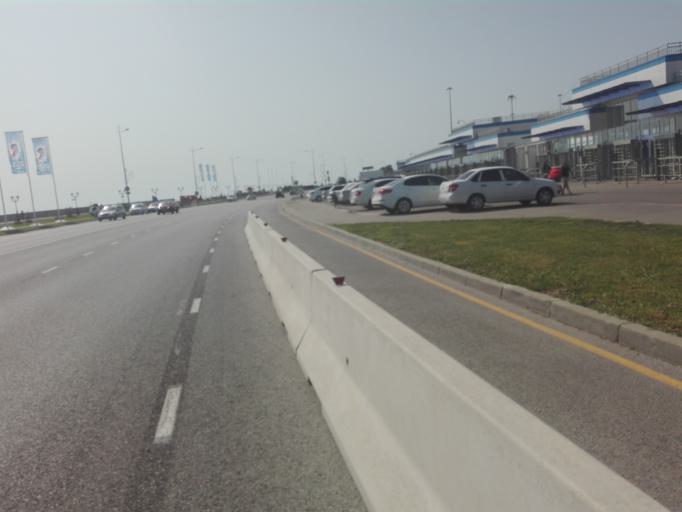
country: RU
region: Krasnodarskiy
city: Adler
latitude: 43.4002
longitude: 39.9571
